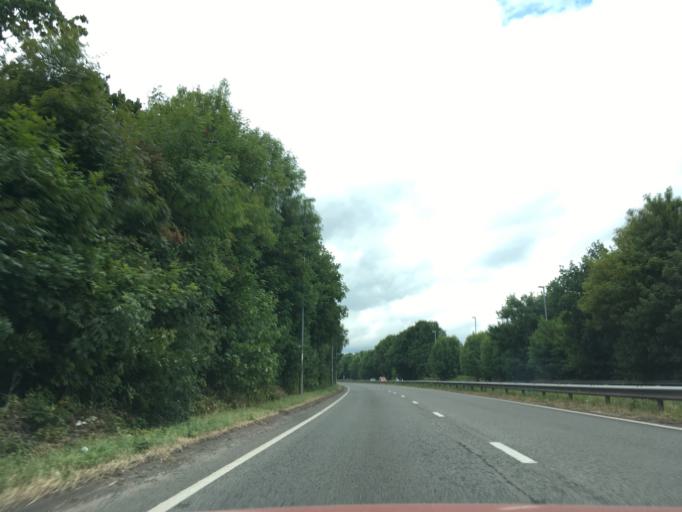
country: GB
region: Wales
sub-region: Torfaen County Borough
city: Cwmbran
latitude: 51.6563
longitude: -2.9988
